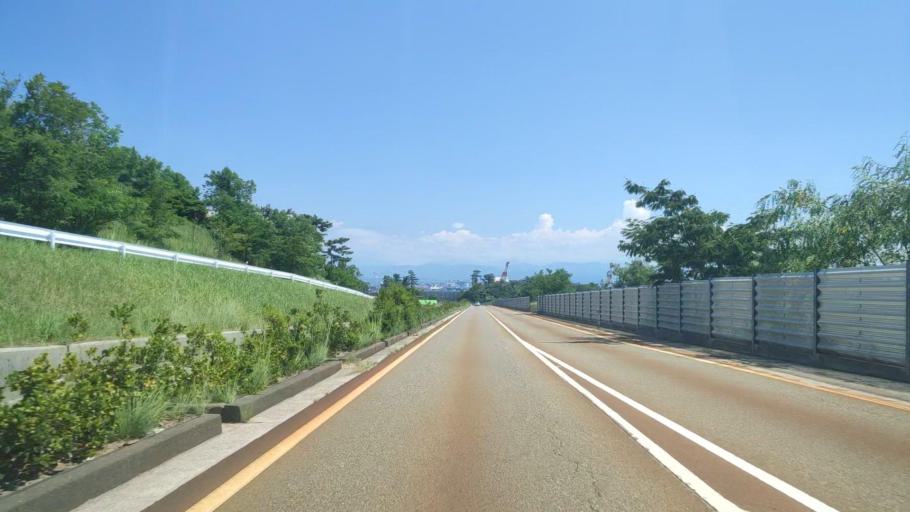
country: JP
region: Ishikawa
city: Kanazawa-shi
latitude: 36.6223
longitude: 136.6174
